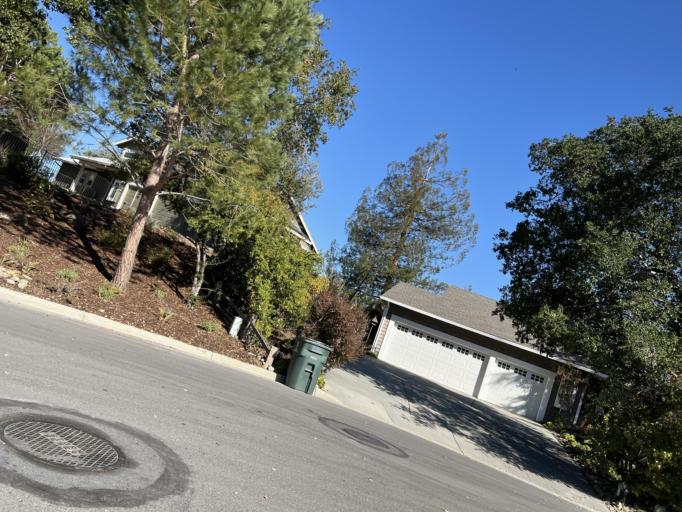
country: US
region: California
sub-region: Santa Clara County
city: Loyola
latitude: 37.3187
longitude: -122.0769
